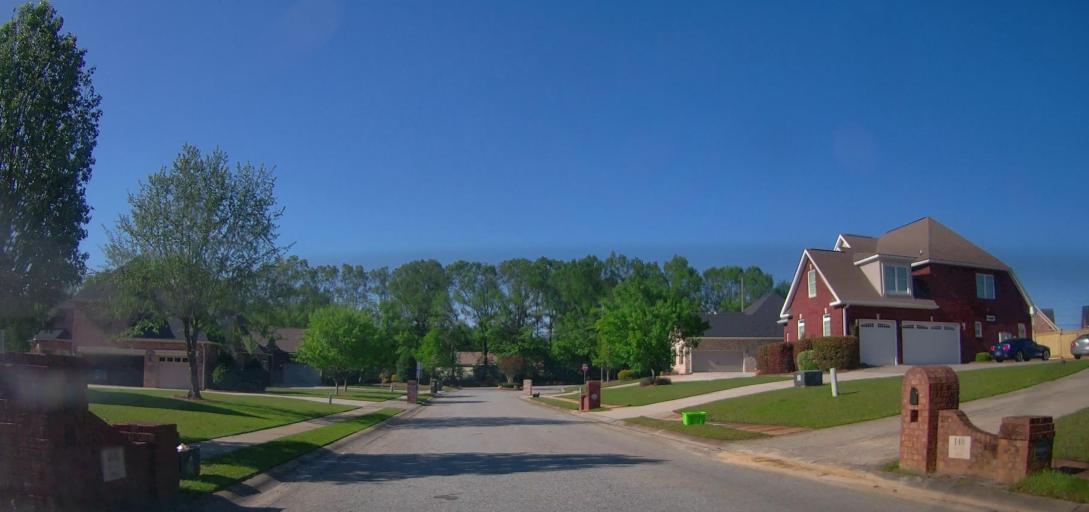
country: US
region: Georgia
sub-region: Houston County
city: Robins Air Force Base
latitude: 32.5428
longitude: -83.5913
